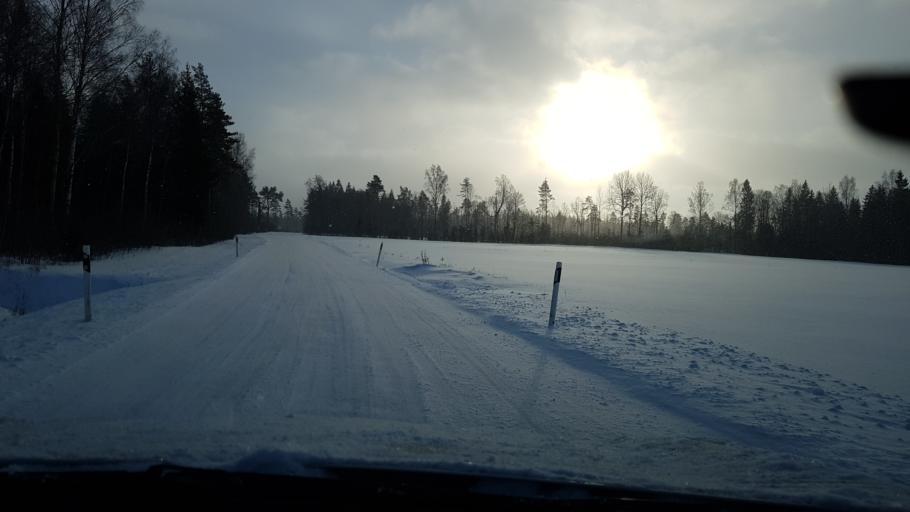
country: EE
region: Harju
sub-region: Nissi vald
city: Turba
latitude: 59.1975
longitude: 24.1387
